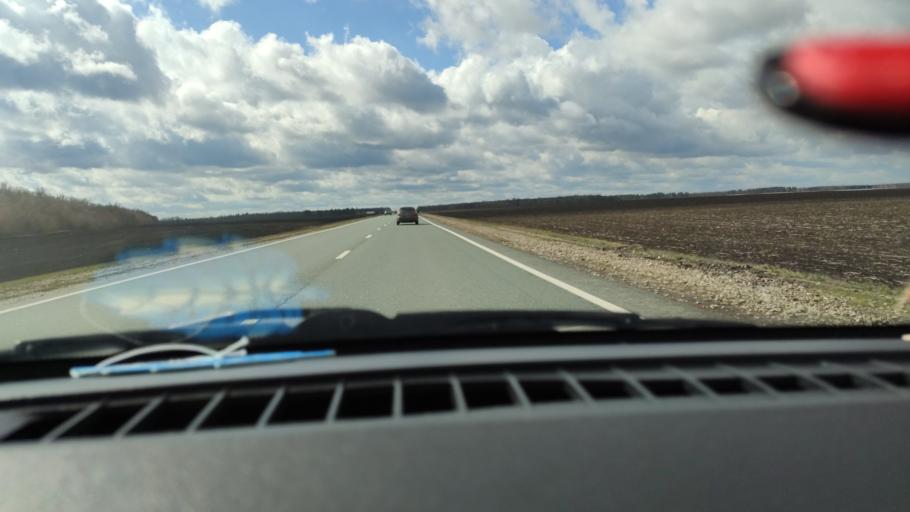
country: RU
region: Samara
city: Yelkhovka
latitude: 53.7646
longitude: 50.2305
